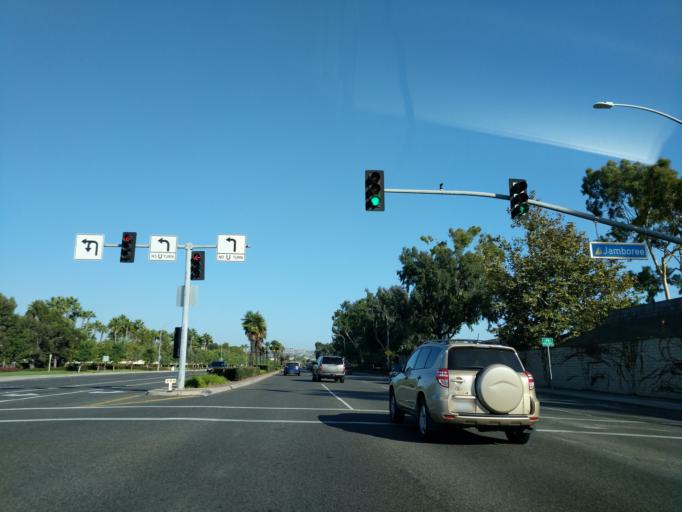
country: US
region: California
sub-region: Orange County
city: Newport Beach
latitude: 33.6127
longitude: -117.8907
